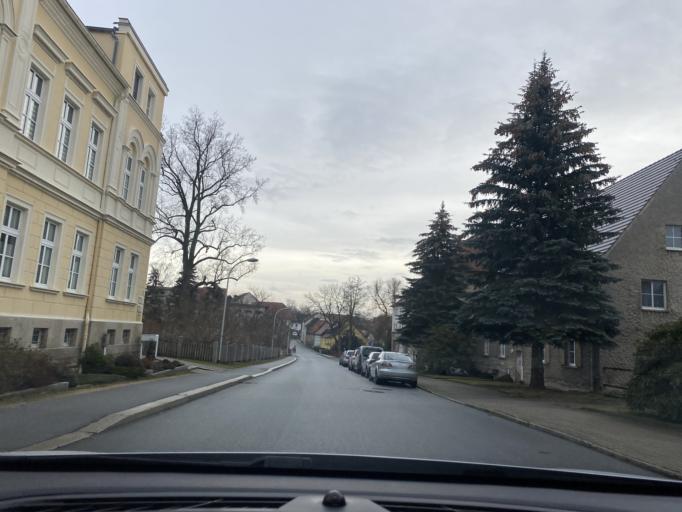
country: DE
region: Saxony
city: Reichenbach
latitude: 51.1428
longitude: 14.7991
